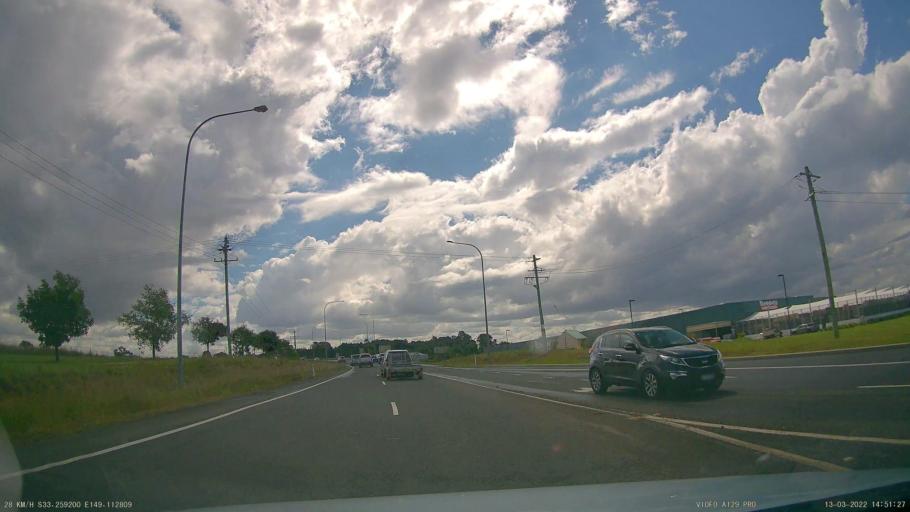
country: AU
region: New South Wales
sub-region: Orange Municipality
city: Orange
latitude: -33.2592
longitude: 149.1128
